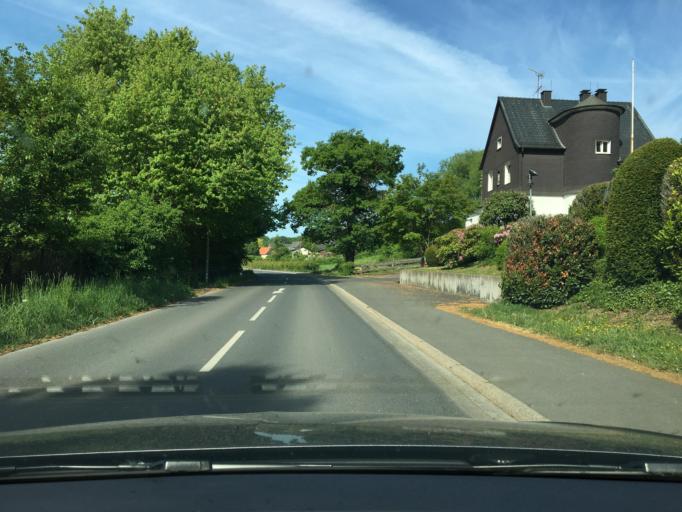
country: DE
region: North Rhine-Westphalia
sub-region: Regierungsbezirk Arnsberg
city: Frondenberg
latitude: 51.4825
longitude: 7.8110
